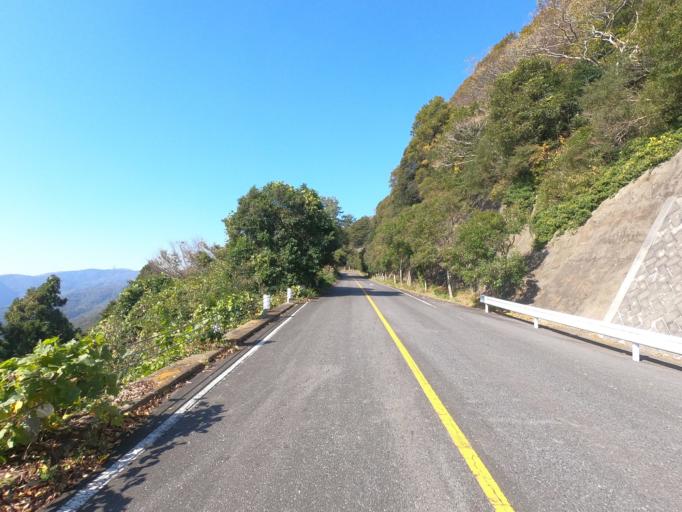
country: JP
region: Ibaraki
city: Tsukuba
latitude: 36.1699
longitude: 140.1739
